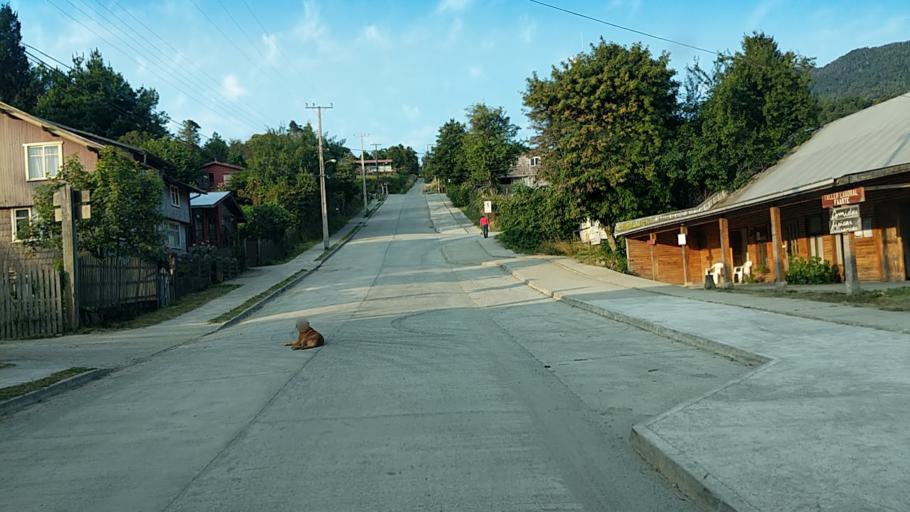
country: CL
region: Los Lagos
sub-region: Provincia de Llanquihue
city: La Ensenada
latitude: -41.4937
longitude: -72.3085
